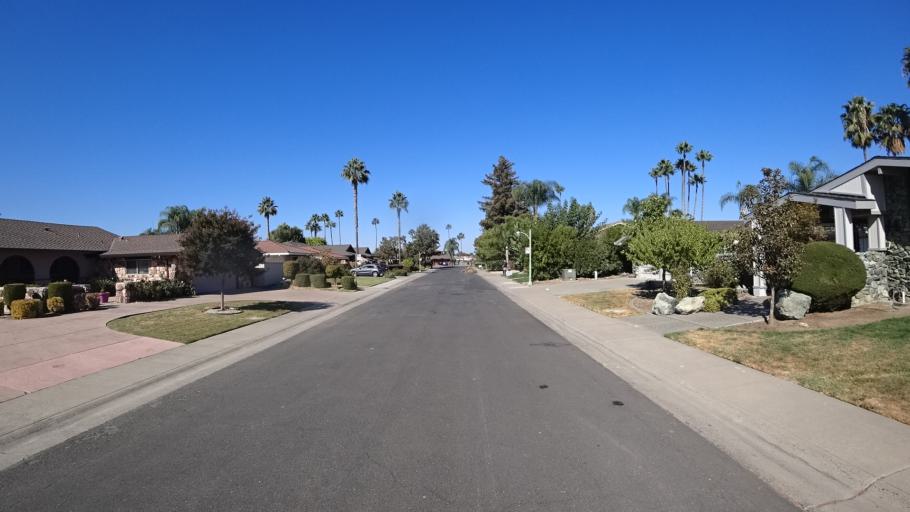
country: US
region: California
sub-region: Yolo County
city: West Sacramento
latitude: 38.5057
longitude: -121.5345
